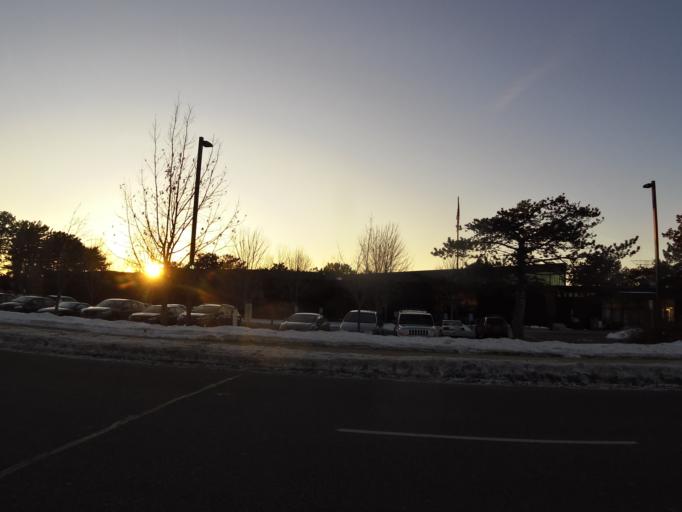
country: US
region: Minnesota
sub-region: Ramsey County
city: North Saint Paul
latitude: 45.0324
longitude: -93.0257
